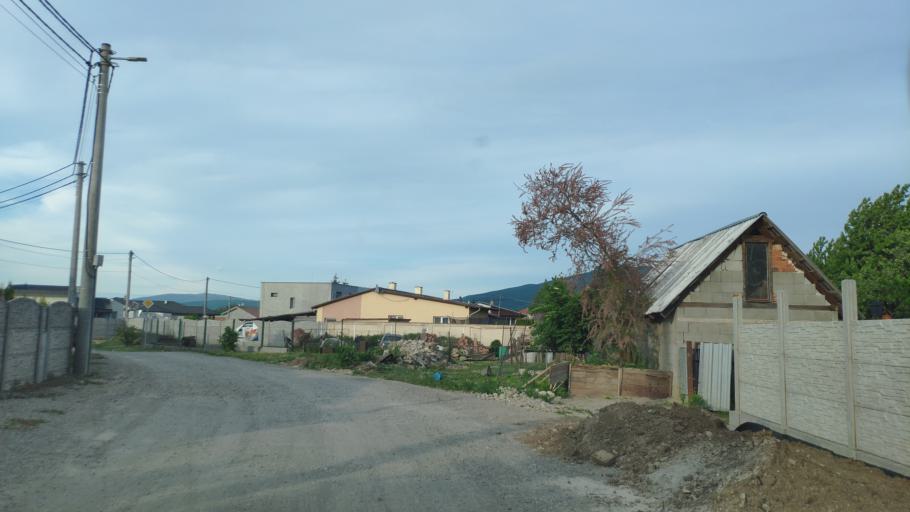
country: SK
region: Kosicky
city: Kosice
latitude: 48.6117
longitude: 21.3298
